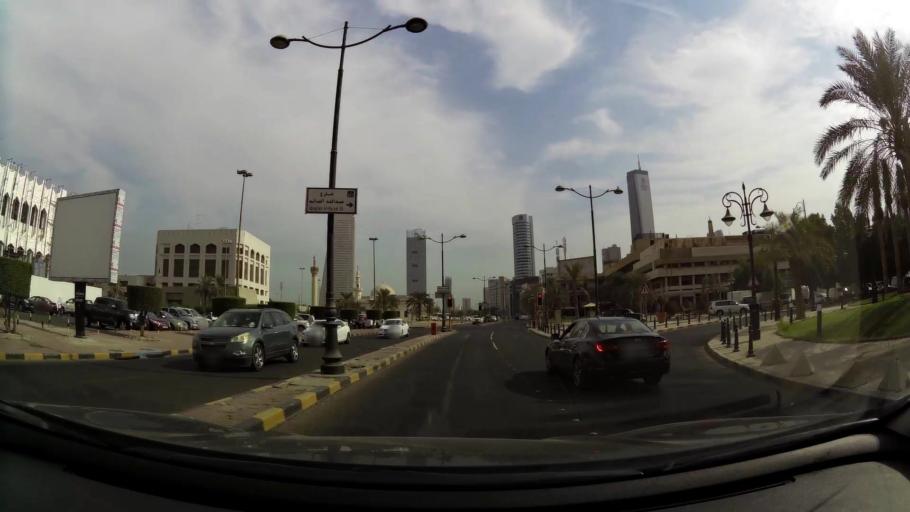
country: KW
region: Al Asimah
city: Kuwait City
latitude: 29.3759
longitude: 47.9709
